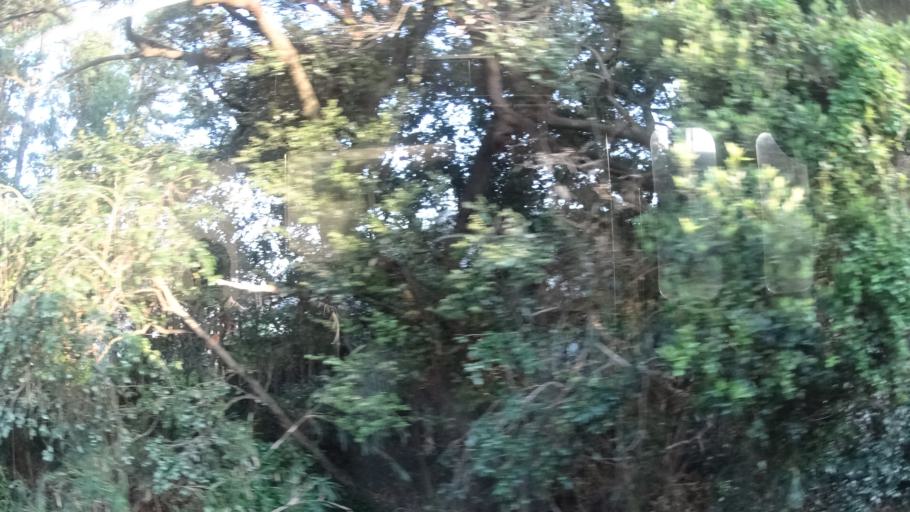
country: JP
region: Aichi
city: Tahara
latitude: 34.6672
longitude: 137.2932
